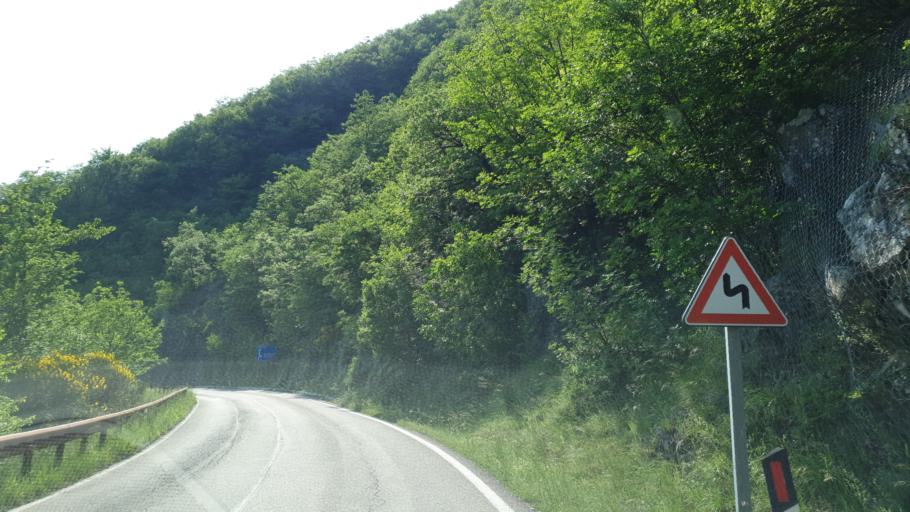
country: IT
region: Tuscany
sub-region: Province of Arezzo
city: Soci
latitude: 43.7718
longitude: 11.8482
